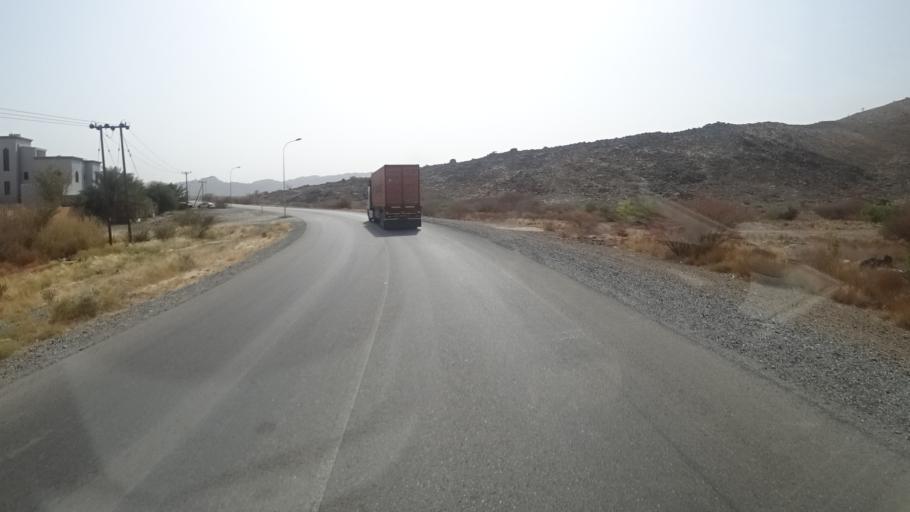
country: OM
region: Muhafazat ad Dakhiliyah
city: Nizwa
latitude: 23.0020
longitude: 57.5531
